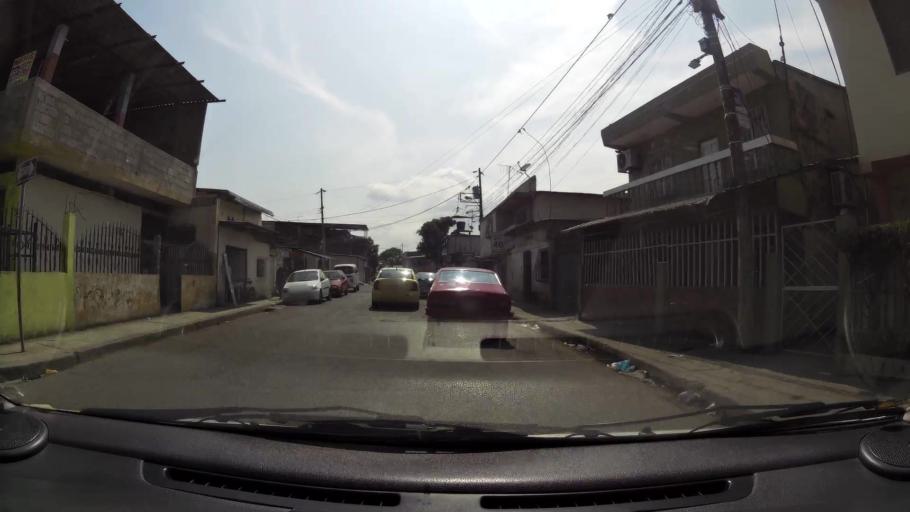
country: EC
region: Guayas
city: Guayaquil
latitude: -2.2637
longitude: -79.8886
